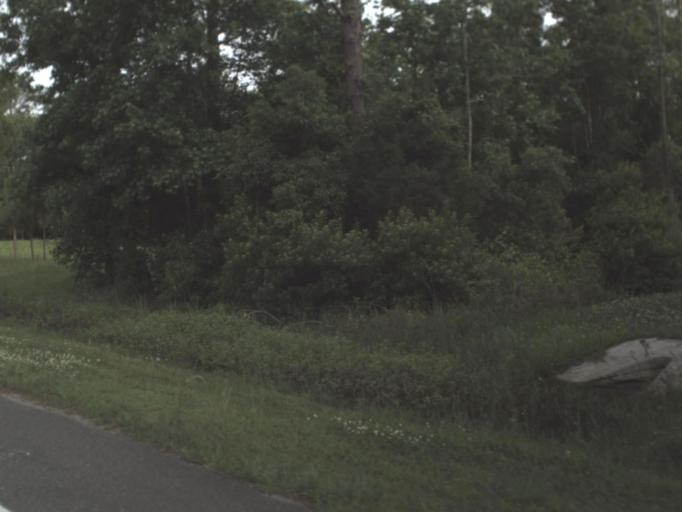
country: US
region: Florida
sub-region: Saint Johns County
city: Saint Augustine
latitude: 29.9599
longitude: -81.4694
